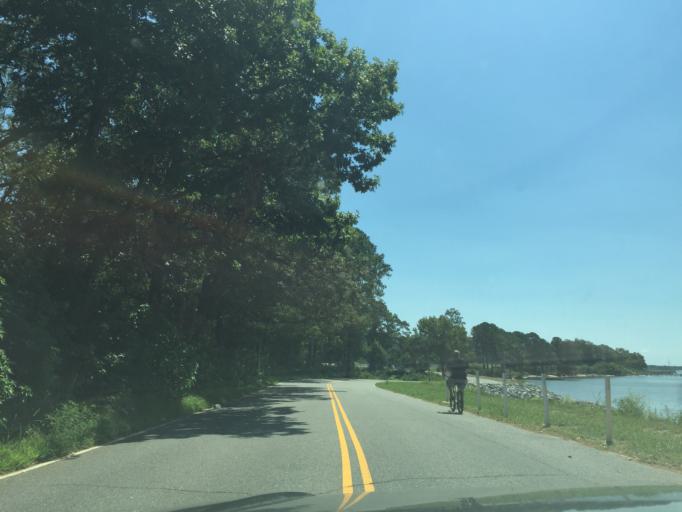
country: US
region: Virginia
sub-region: City of Newport News
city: Newport News
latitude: 37.0425
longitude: -76.4908
